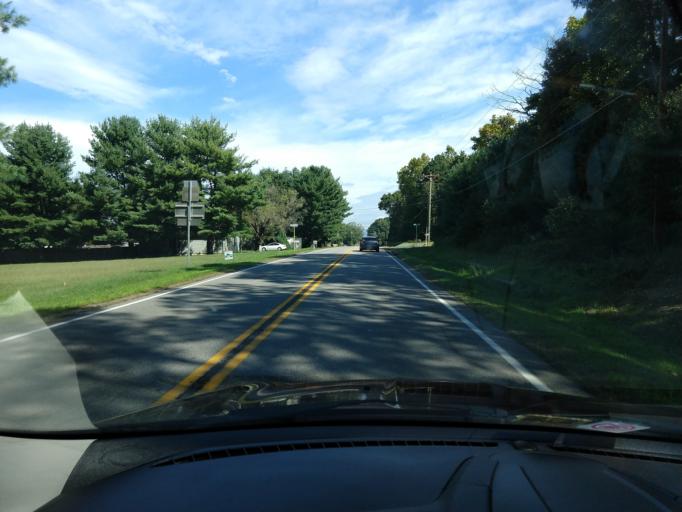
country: US
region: Virginia
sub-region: Rockingham County
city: Grottoes
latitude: 38.2545
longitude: -78.8228
